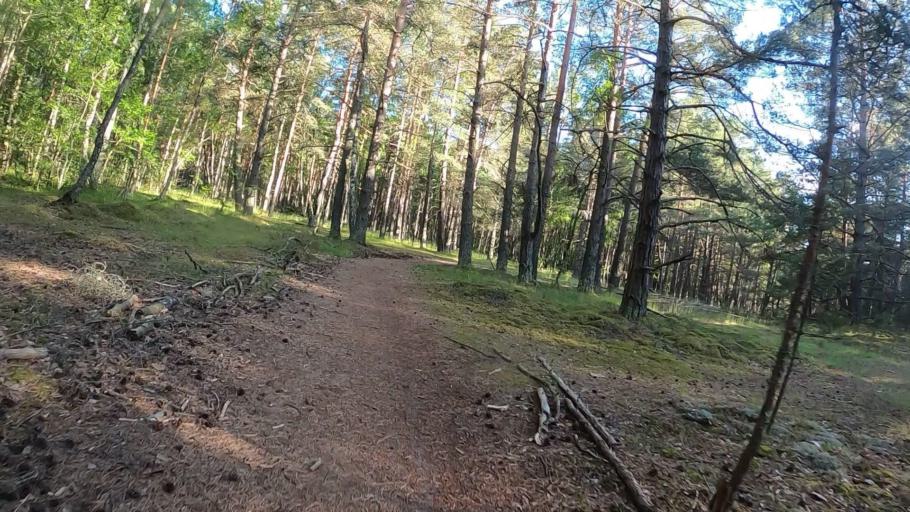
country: LV
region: Carnikava
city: Carnikava
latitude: 57.1359
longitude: 24.2350
